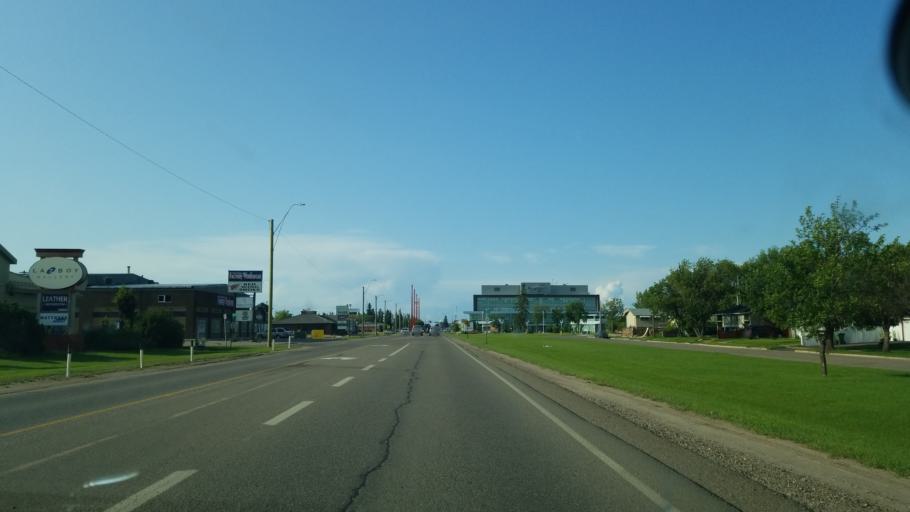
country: CA
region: Saskatchewan
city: Lloydminster
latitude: 53.2737
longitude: -110.0054
